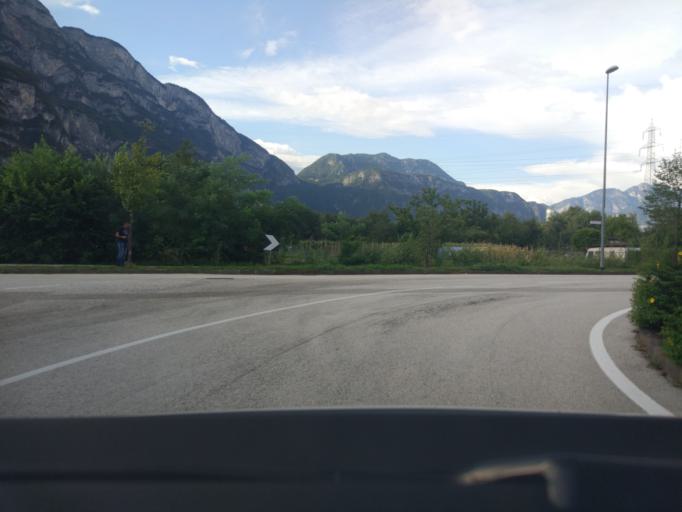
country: IT
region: Trentino-Alto Adige
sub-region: Provincia di Trento
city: Lavis
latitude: 46.1218
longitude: 11.0902
